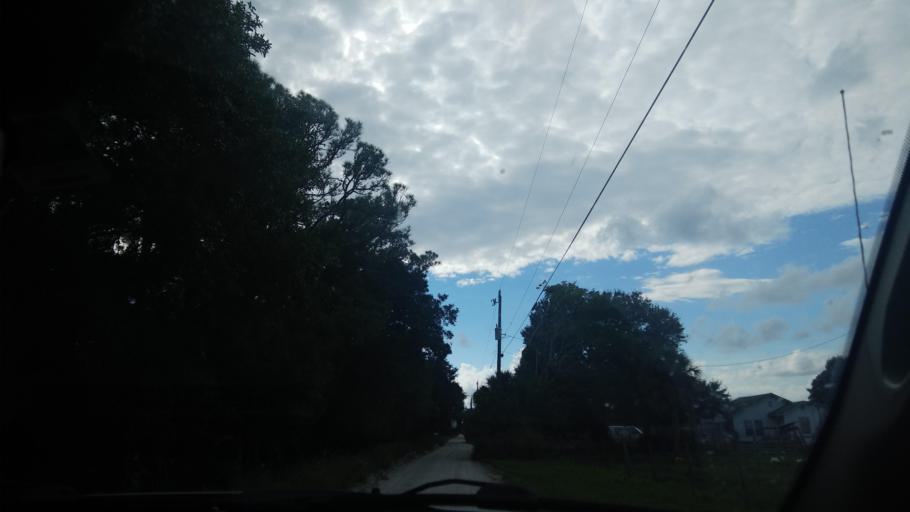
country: US
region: Florida
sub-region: Indian River County
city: Fellsmere
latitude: 27.7864
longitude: -80.5964
